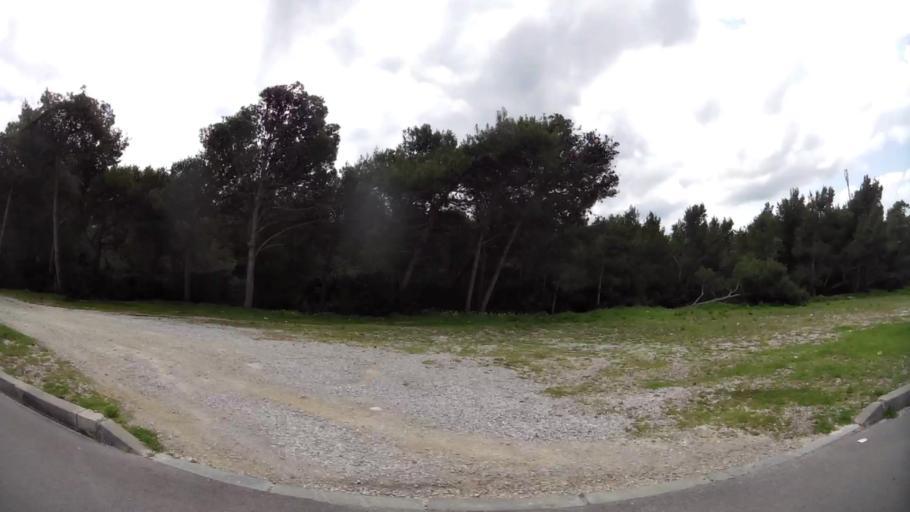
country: MA
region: Tanger-Tetouan
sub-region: Tanger-Assilah
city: Tangier
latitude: 35.7921
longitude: -5.7538
